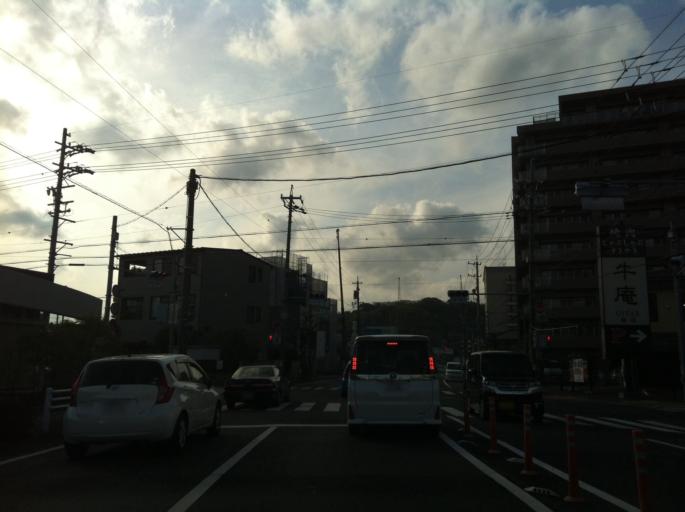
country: JP
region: Shizuoka
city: Shizuoka-shi
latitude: 34.9777
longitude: 138.4106
